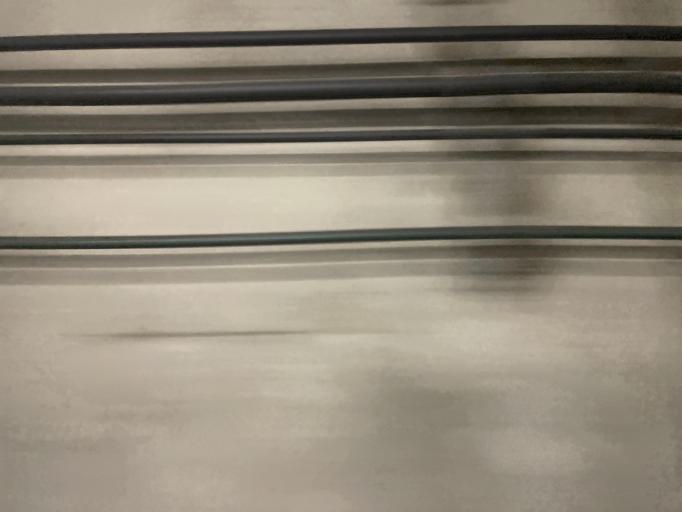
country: JP
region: Gunma
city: Nakanojomachi
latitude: 36.5362
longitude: 138.6758
